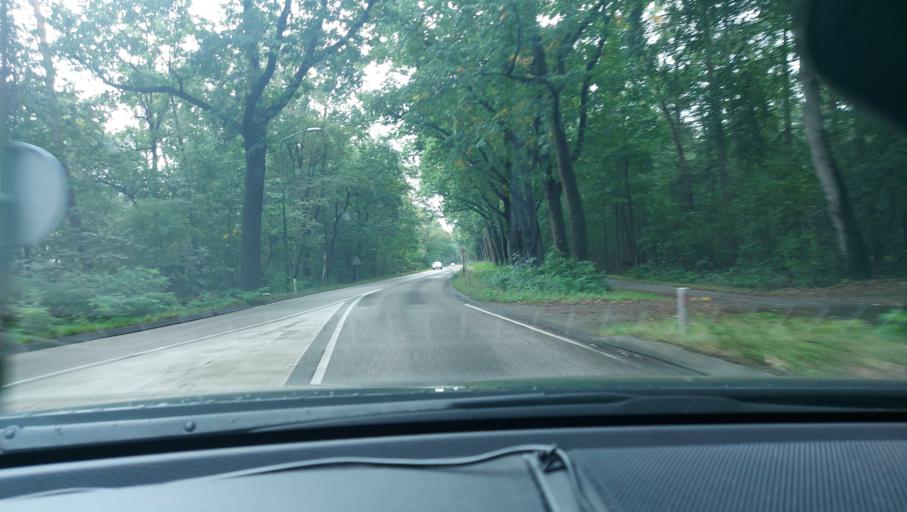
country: NL
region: North Brabant
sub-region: Gemeente Sint Anthonis
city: Sint Anthonis
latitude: 51.5405
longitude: 5.8010
